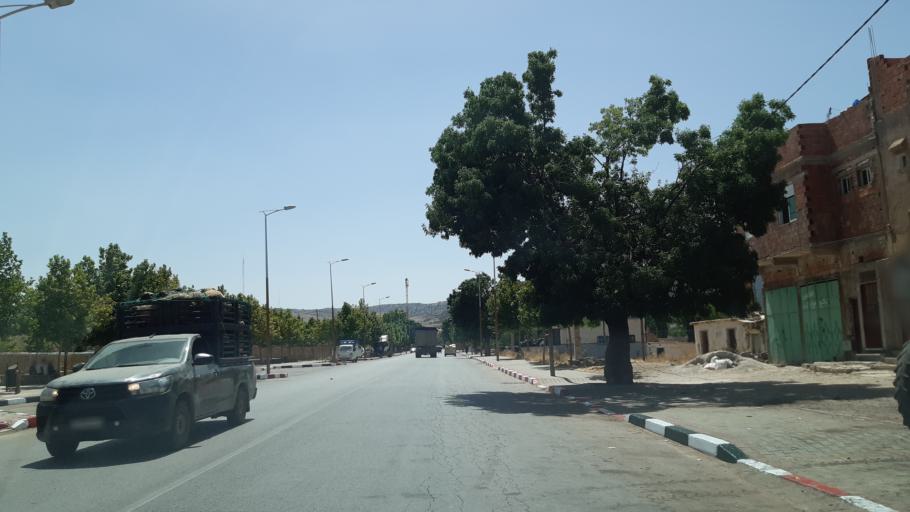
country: MA
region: Meknes-Tafilalet
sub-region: Ifrane
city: Azrou
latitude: 33.2385
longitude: -5.0633
